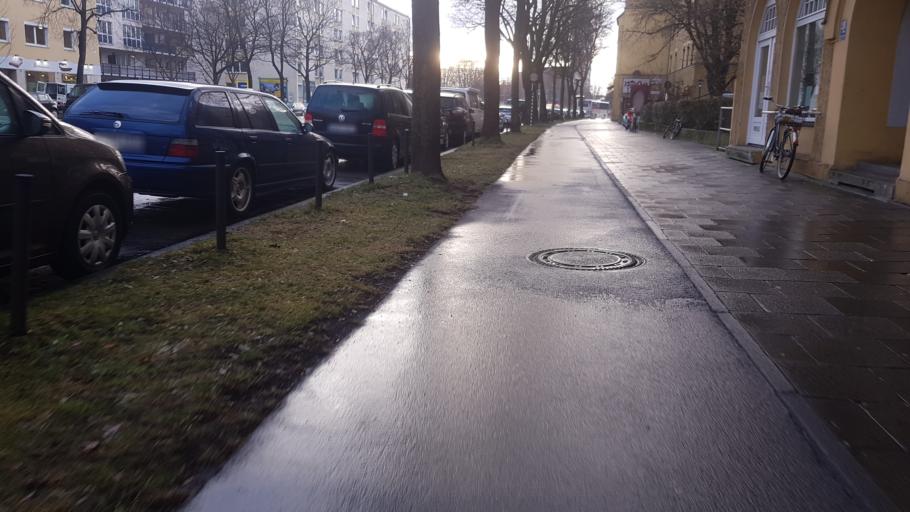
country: DE
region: Bavaria
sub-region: Upper Bavaria
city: Bogenhausen
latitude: 48.1166
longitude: 11.6117
